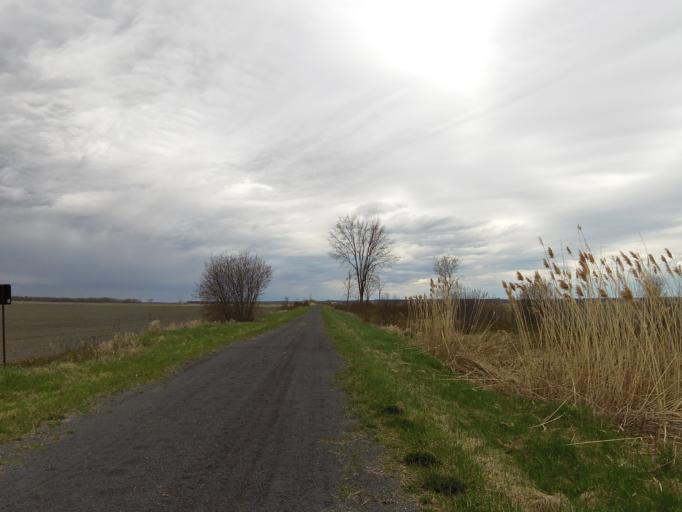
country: CA
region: Quebec
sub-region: Outaouais
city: Papineauville
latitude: 45.5426
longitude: -74.8227
